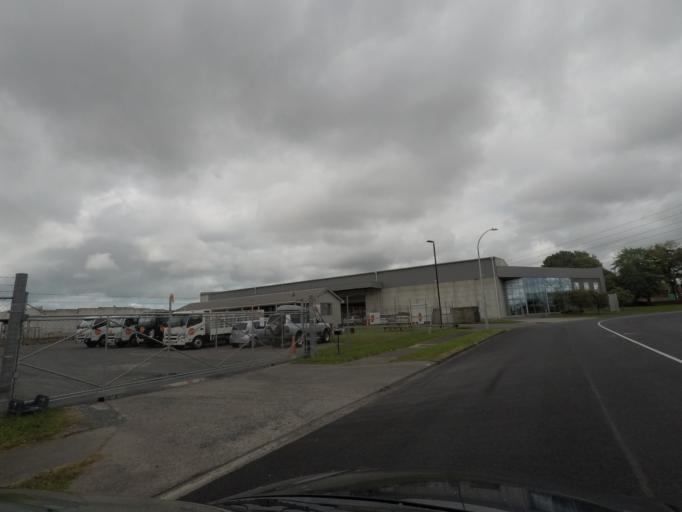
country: NZ
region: Auckland
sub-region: Auckland
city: Tamaki
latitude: -36.9342
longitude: 174.8850
